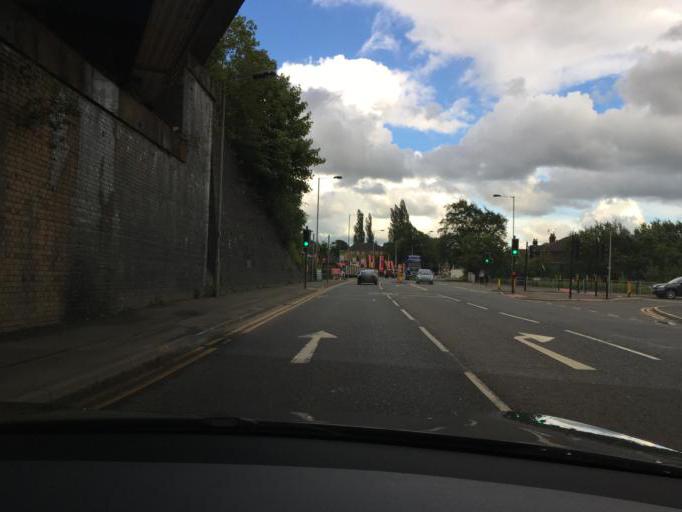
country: GB
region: England
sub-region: Borough of Stockport
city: Hazel Grove
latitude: 53.3746
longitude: -2.1107
